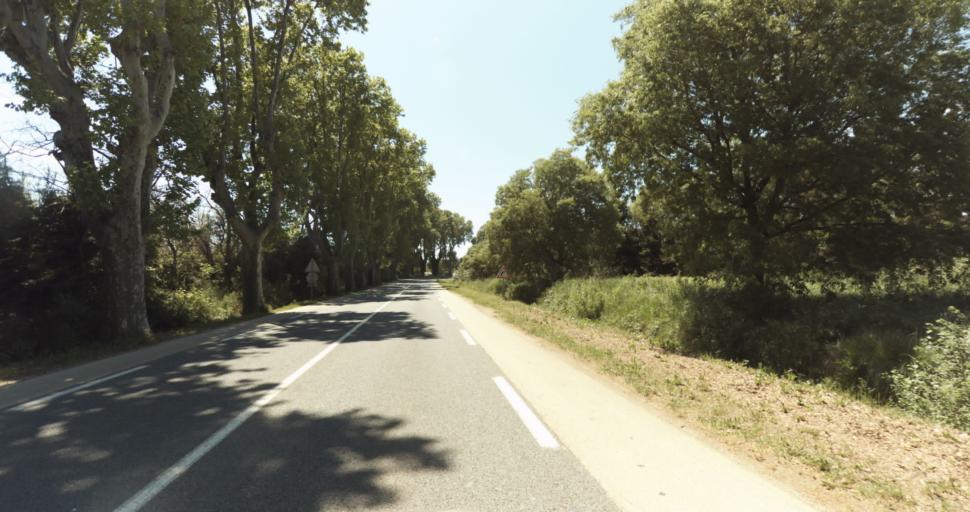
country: FR
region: Provence-Alpes-Cote d'Azur
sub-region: Departement du Var
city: Hyeres
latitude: 43.1314
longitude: 6.1703
